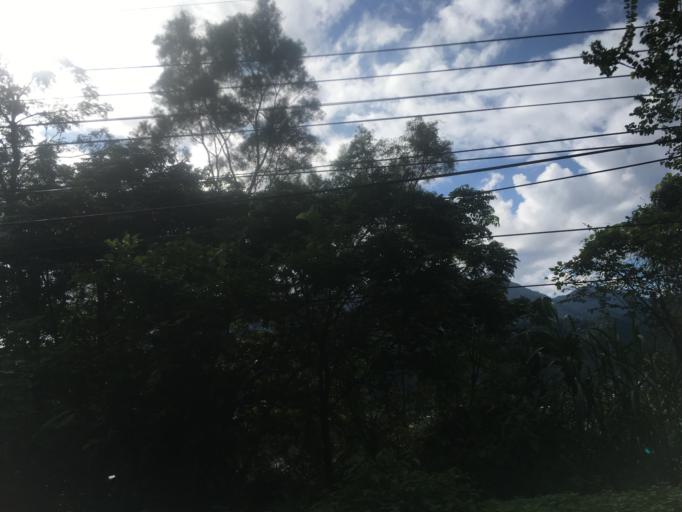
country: TW
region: Taiwan
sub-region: Yilan
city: Yilan
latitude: 24.6485
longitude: 121.5725
